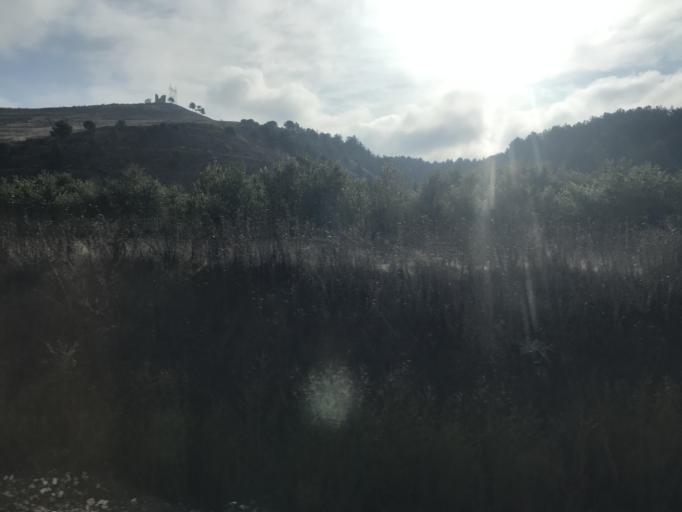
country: ES
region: Castille and Leon
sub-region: Provincia de Burgos
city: Pradanos de Bureba
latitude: 42.5139
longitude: -3.3397
